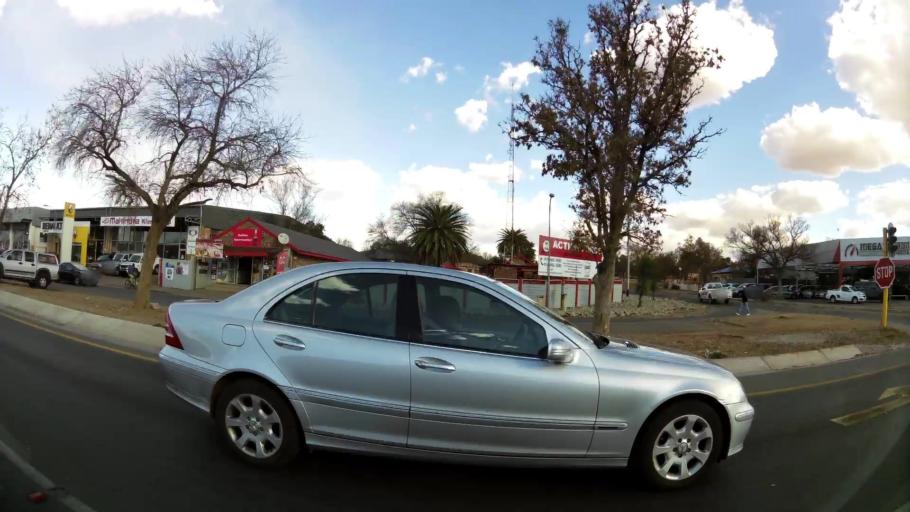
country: ZA
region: North-West
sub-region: Dr Kenneth Kaunda District Municipality
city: Klerksdorp
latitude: -26.8647
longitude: 26.6460
